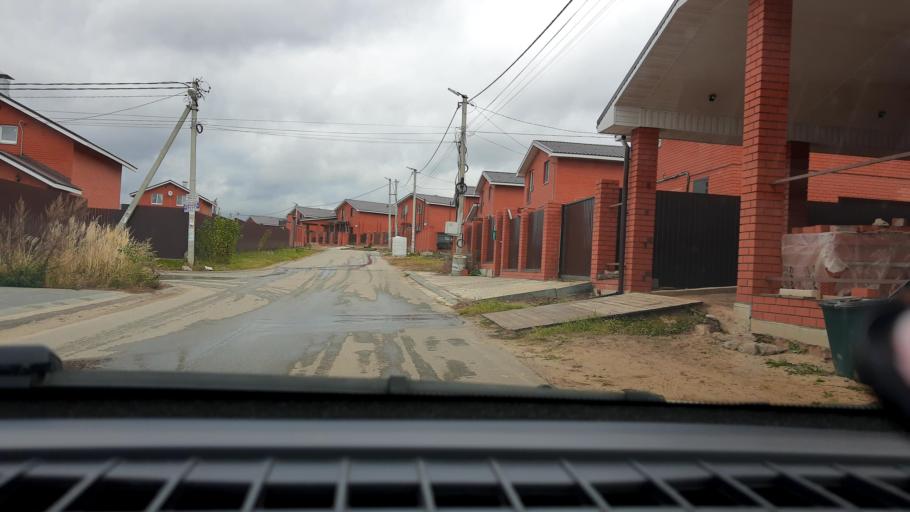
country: RU
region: Nizjnij Novgorod
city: Afonino
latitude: 56.2049
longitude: 44.1394
